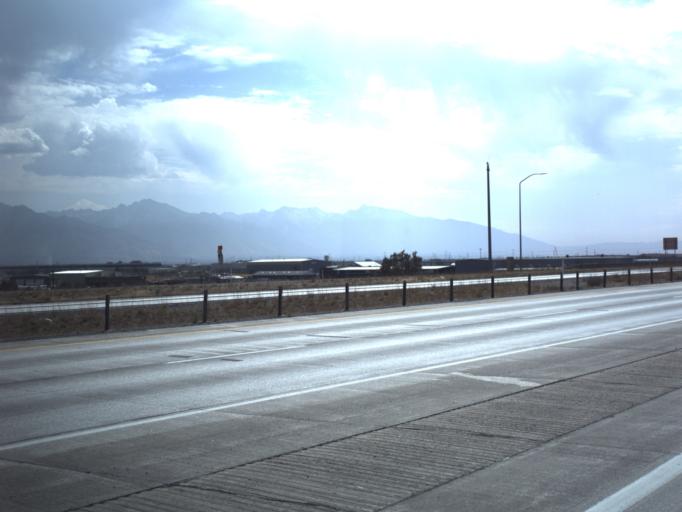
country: US
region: Utah
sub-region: Salt Lake County
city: West Valley City
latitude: 40.7599
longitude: -111.9871
